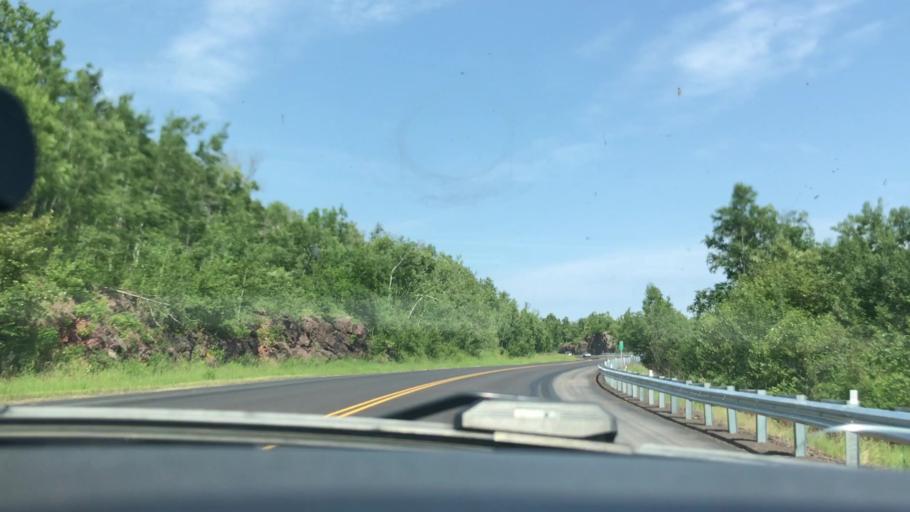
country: US
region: Minnesota
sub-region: Lake County
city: Silver Bay
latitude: 47.3675
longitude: -91.1706
